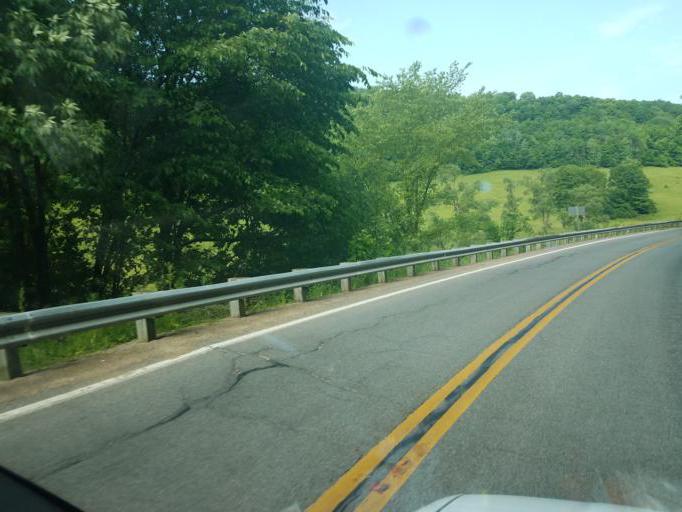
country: US
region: Wisconsin
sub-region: Vernon County
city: Hillsboro
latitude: 43.6743
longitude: -90.4964
